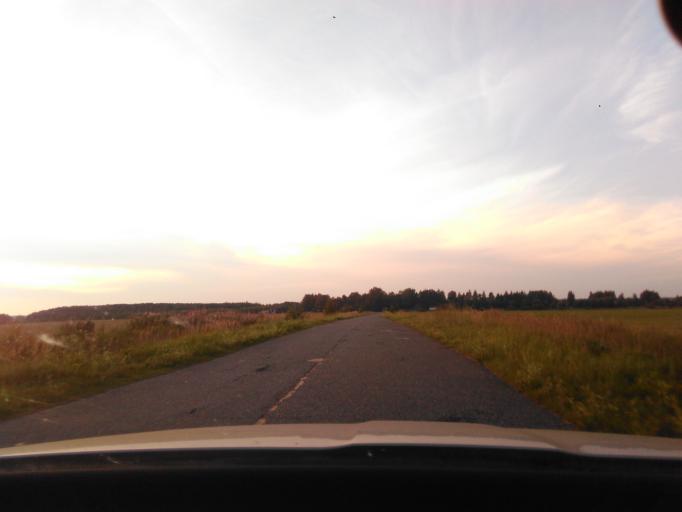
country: RU
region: Tverskaya
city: Zavidovo
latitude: 56.6041
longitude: 36.5947
